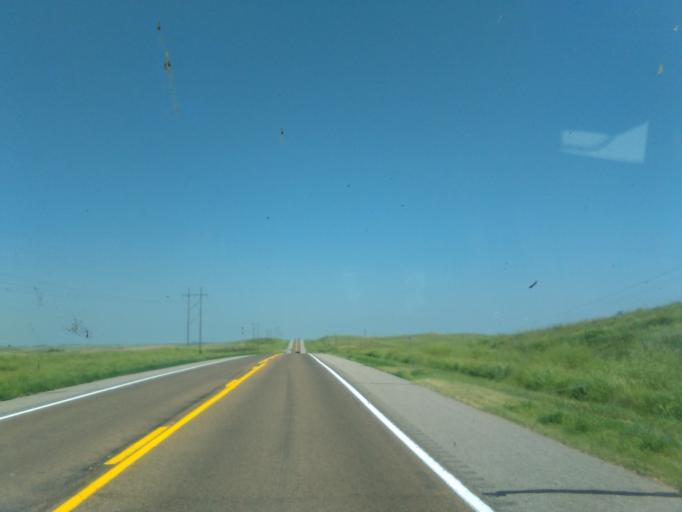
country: US
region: Nebraska
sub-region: Lincoln County
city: North Platte
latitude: 40.8400
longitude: -100.7539
